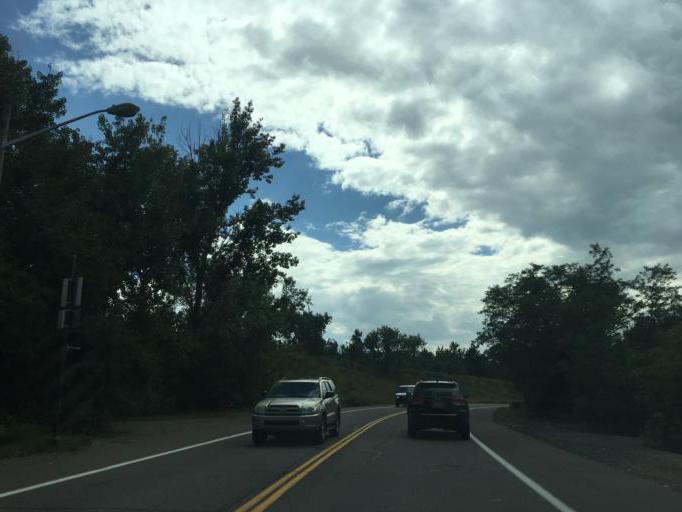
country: US
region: Colorado
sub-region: Jefferson County
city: Applewood
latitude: 39.7404
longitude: -105.1441
